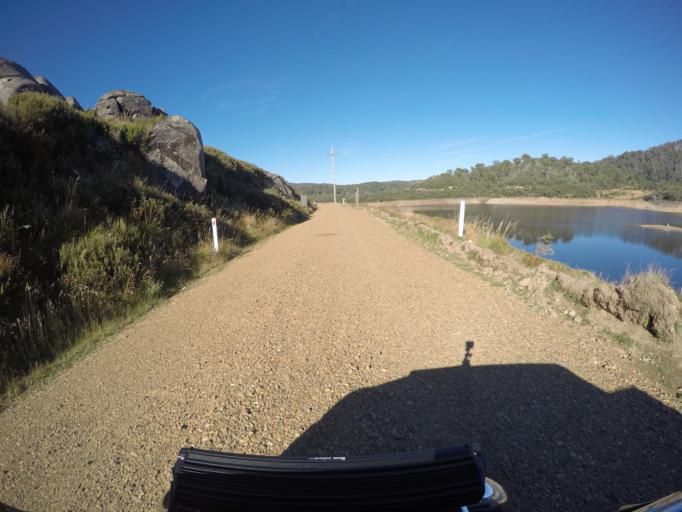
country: AU
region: New South Wales
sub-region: Snowy River
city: Jindabyne
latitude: -36.0539
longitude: 148.2791
